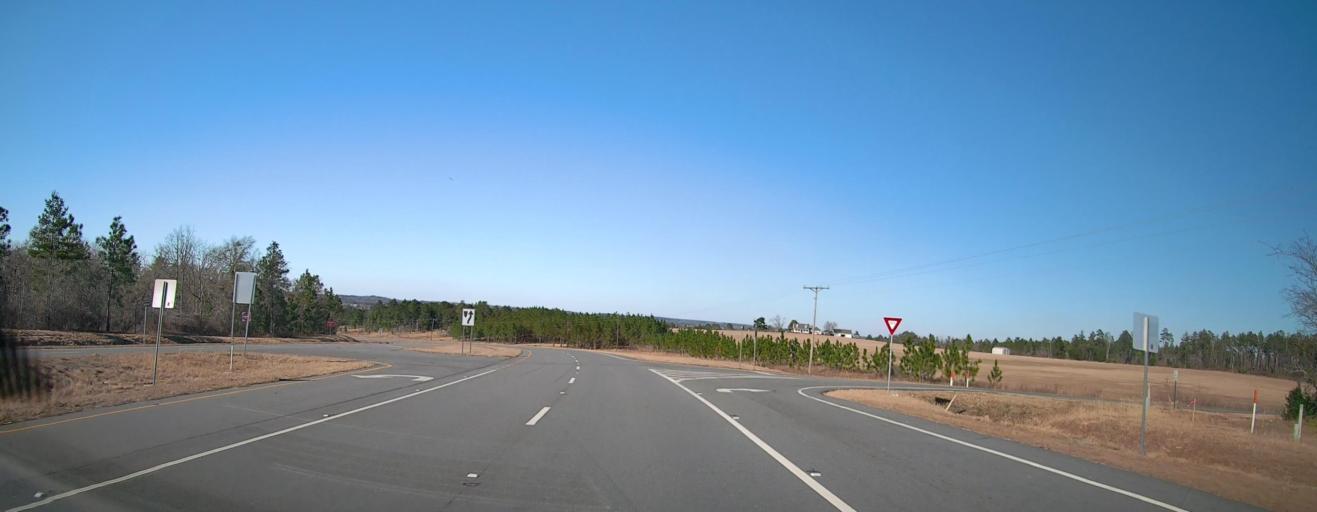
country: US
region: Georgia
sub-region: Taylor County
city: Butler
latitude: 32.6085
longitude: -84.2374
